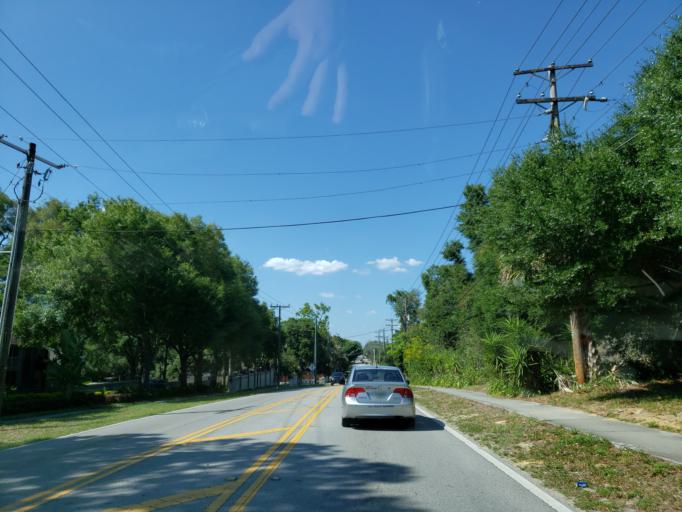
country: US
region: Florida
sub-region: Hillsborough County
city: Brandon
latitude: 27.9440
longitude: -82.3103
